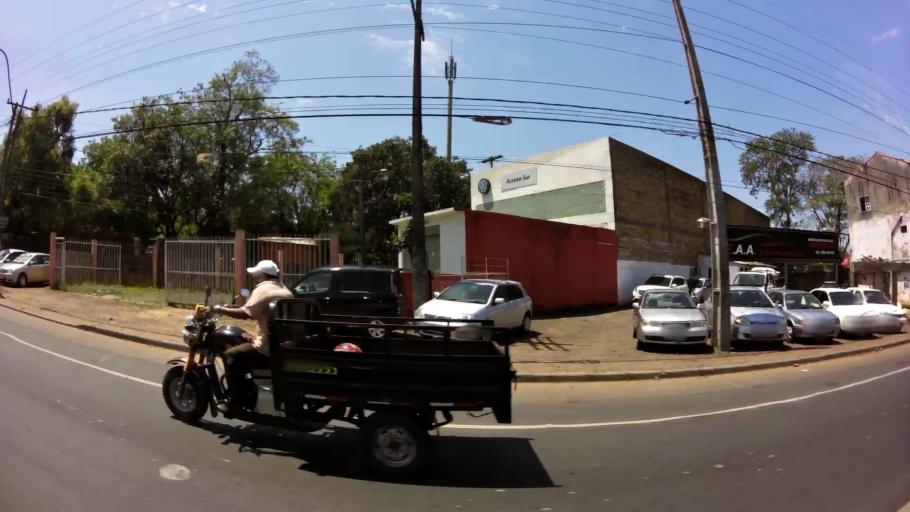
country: PY
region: Central
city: Nemby
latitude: -25.3764
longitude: -57.5557
